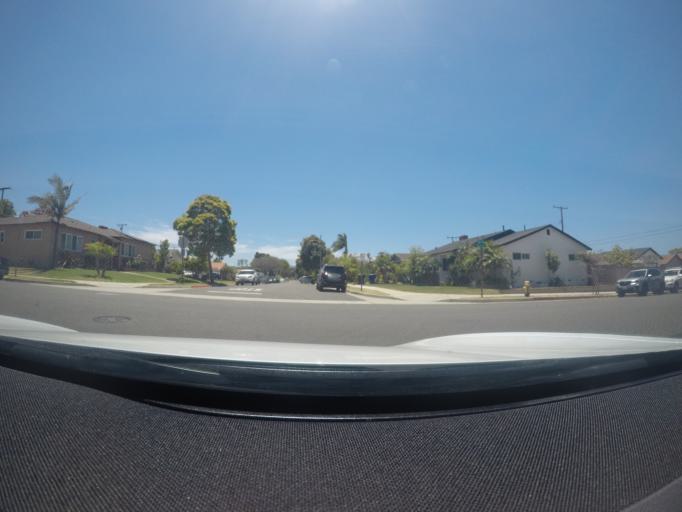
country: US
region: California
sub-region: Los Angeles County
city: Torrance
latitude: 33.8466
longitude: -118.3430
